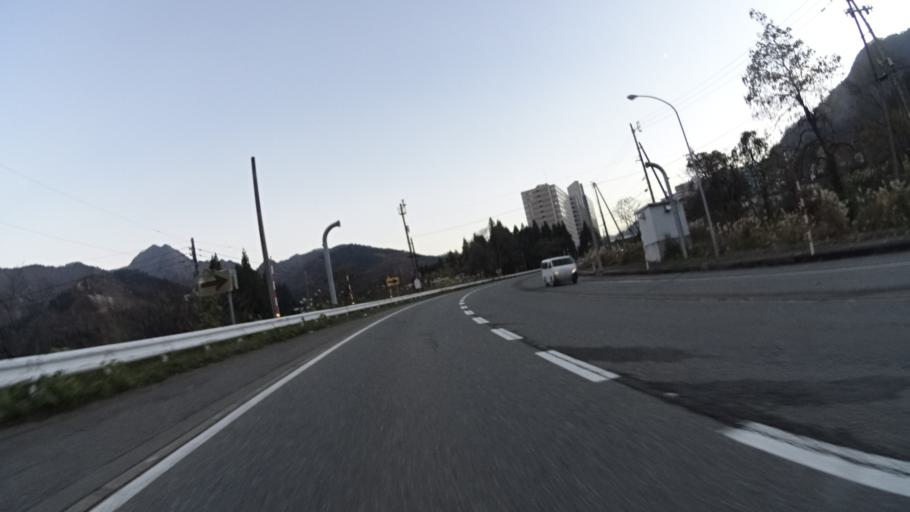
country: JP
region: Niigata
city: Shiozawa
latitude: 36.9712
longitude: 138.8017
